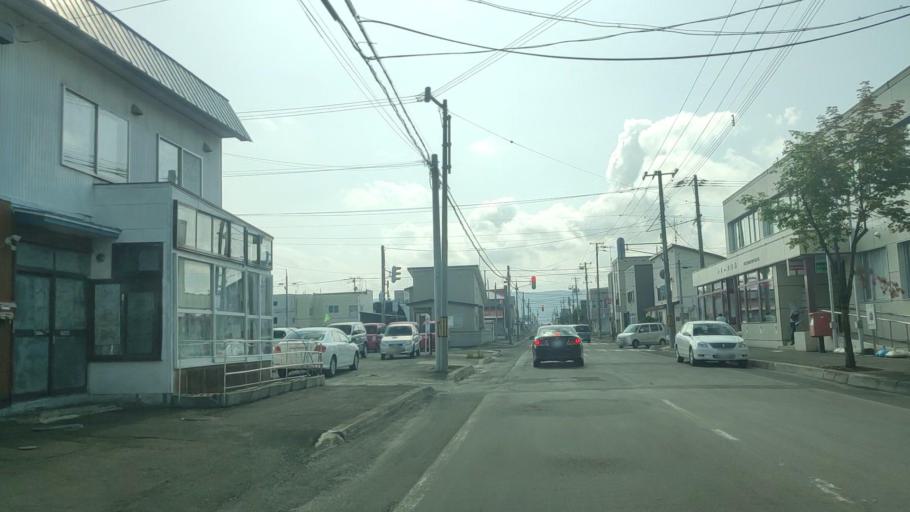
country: JP
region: Hokkaido
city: Shimo-furano
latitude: 43.3461
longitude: 142.3851
